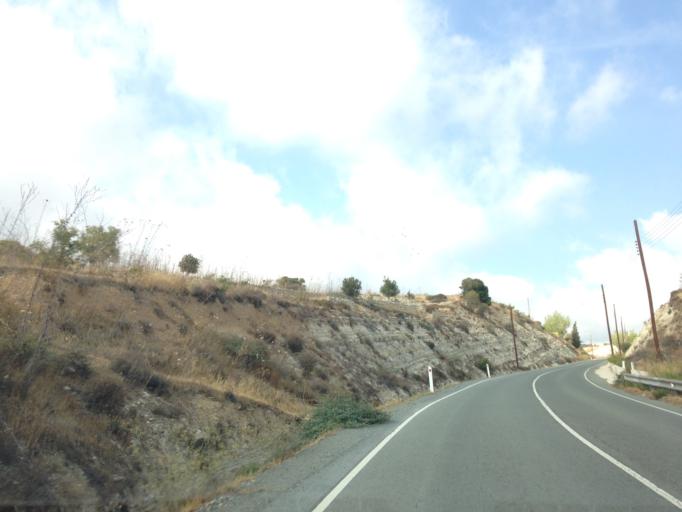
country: CY
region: Limassol
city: Pachna
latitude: 34.8210
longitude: 32.7976
